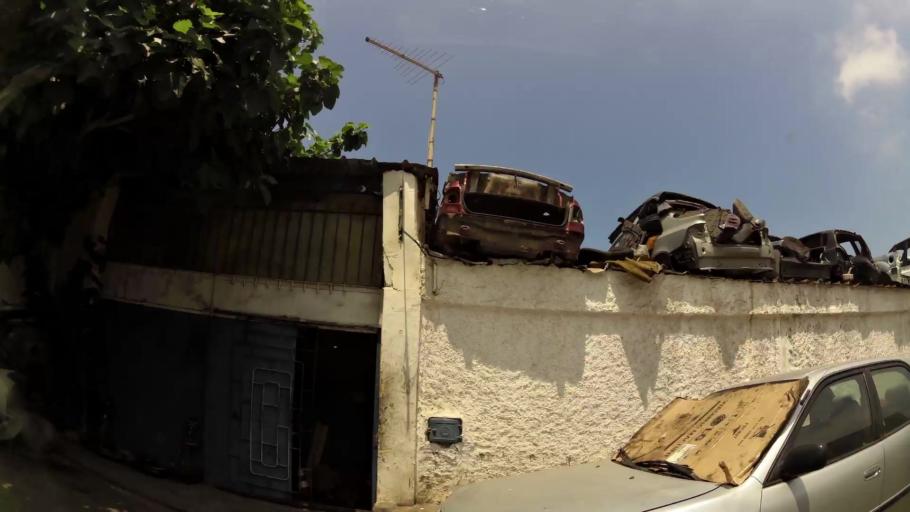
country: MA
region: Rabat-Sale-Zemmour-Zaer
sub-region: Skhirate-Temara
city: Temara
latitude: 33.9818
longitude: -6.8883
